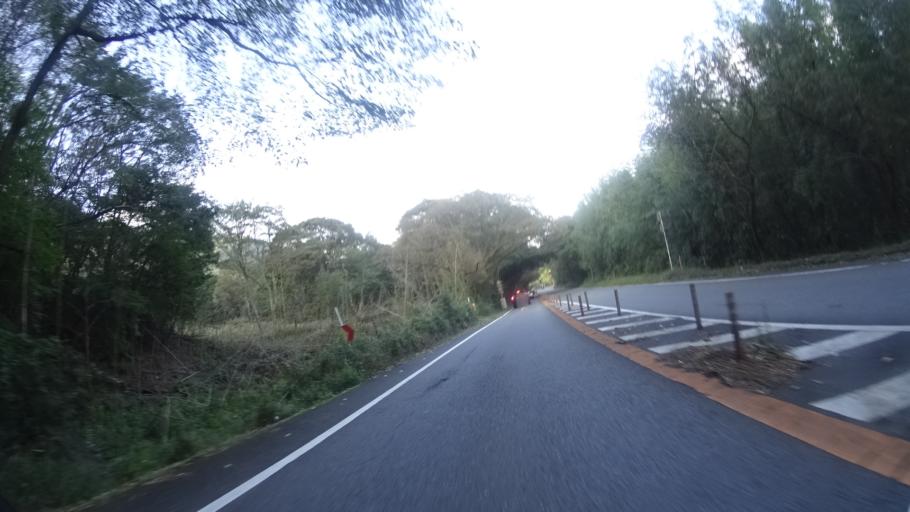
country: JP
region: Oita
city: Beppu
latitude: 33.2734
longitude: 131.4432
